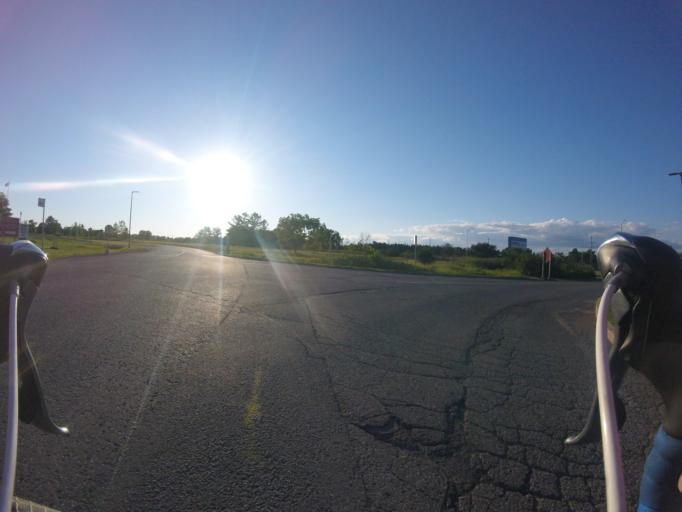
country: CA
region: Ontario
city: Bells Corners
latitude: 45.3536
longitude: -75.8502
